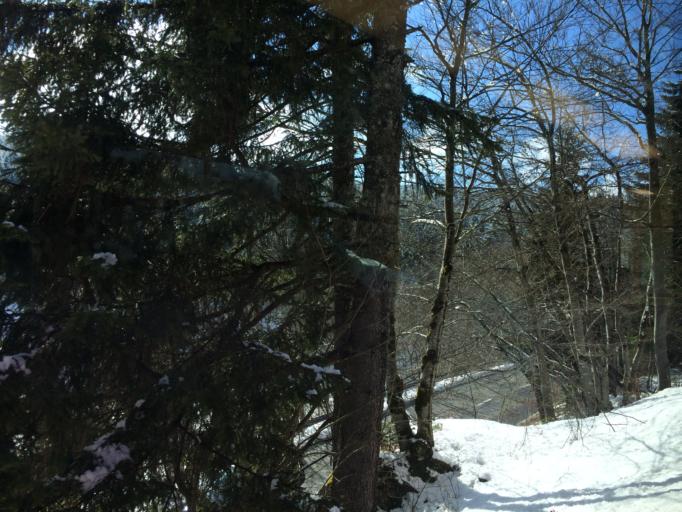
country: CH
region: Vaud
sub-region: Nyon District
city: Saint-Cergue
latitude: 46.4474
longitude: 6.1462
